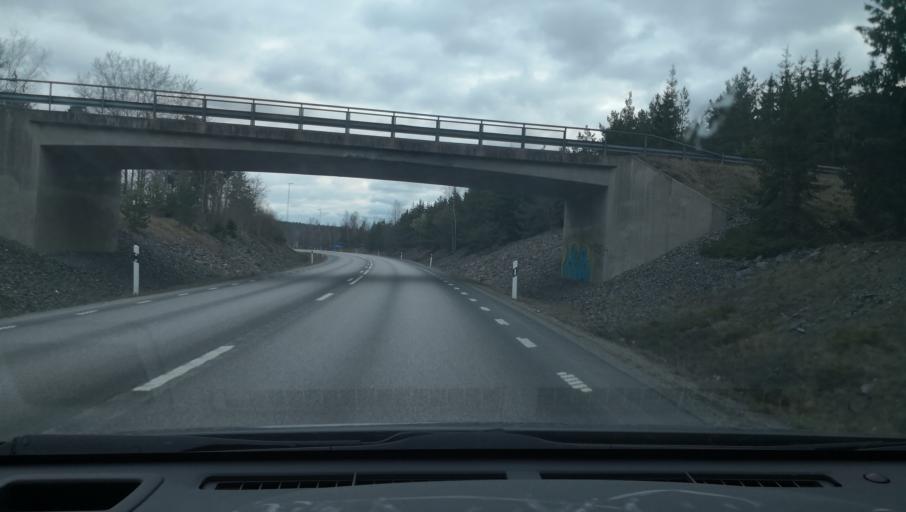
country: SE
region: Soedermanland
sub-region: Strangnas Kommun
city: Strangnas
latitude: 59.3903
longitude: 16.9920
